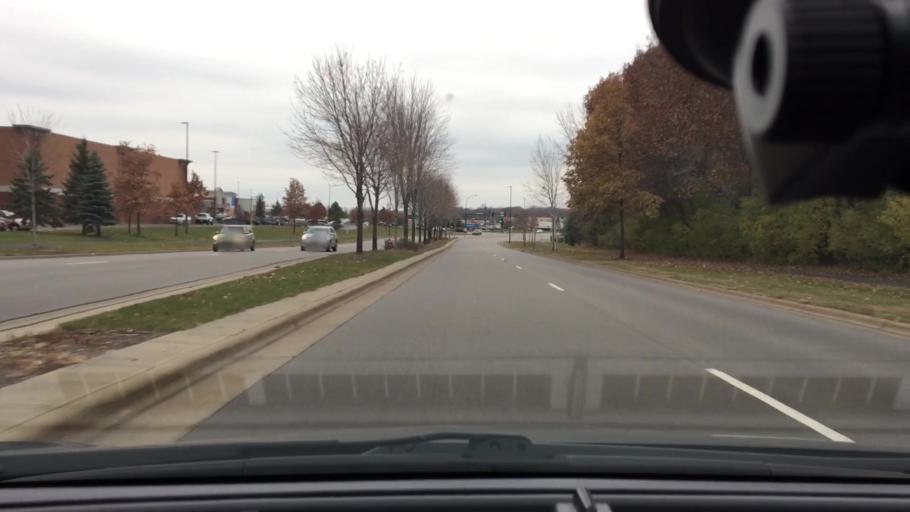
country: US
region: Minnesota
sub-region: Hennepin County
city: Corcoran
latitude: 45.1222
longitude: -93.4923
